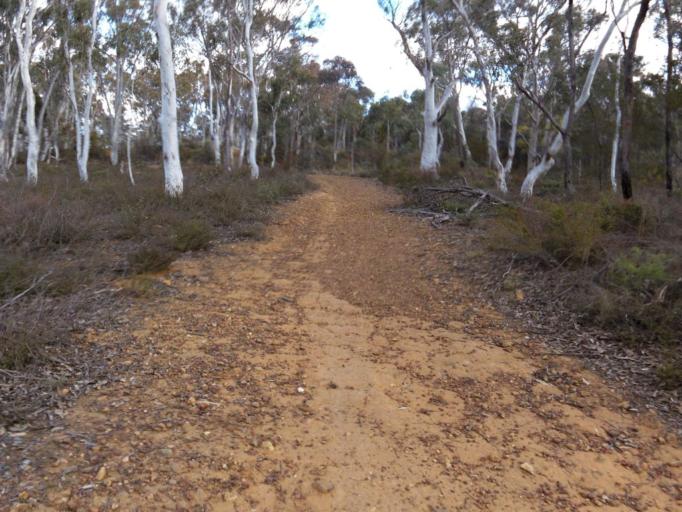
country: AU
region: Australian Capital Territory
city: Acton
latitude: -35.2603
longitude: 149.1094
